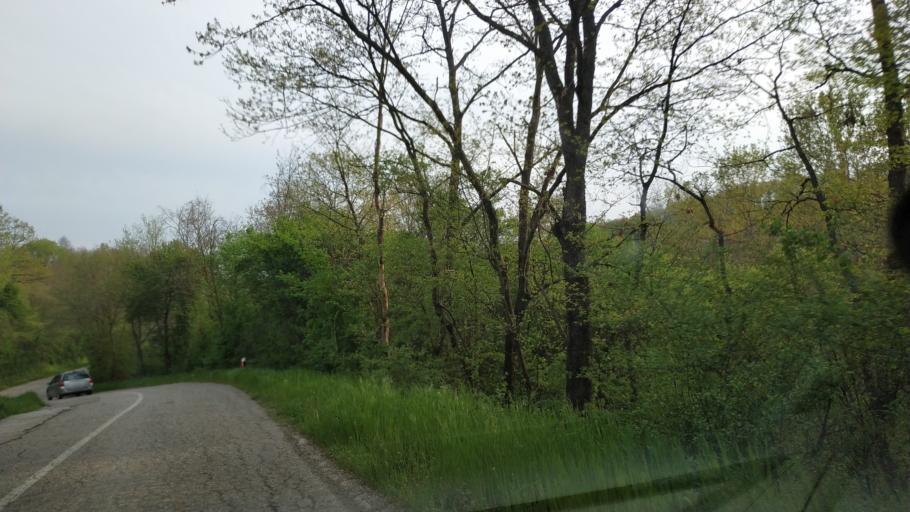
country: RS
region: Central Serbia
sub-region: Nisavski Okrug
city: Aleksinac
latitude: 43.4778
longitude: 21.8108
